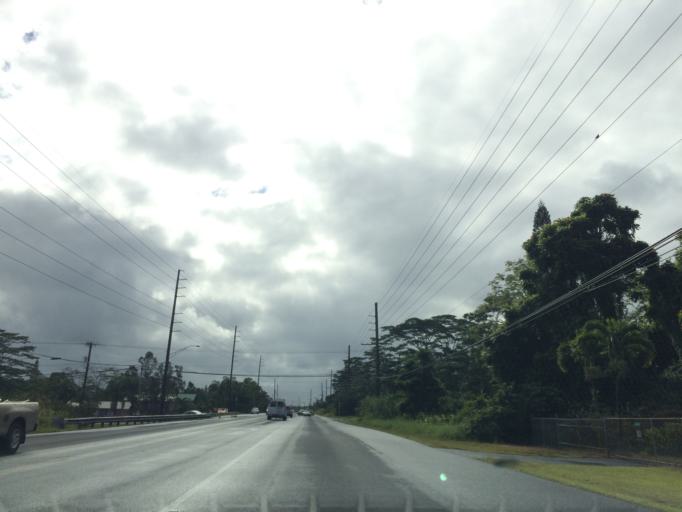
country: US
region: Hawaii
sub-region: Hawaii County
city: Orchidlands Estates
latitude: 19.5586
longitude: -154.9908
